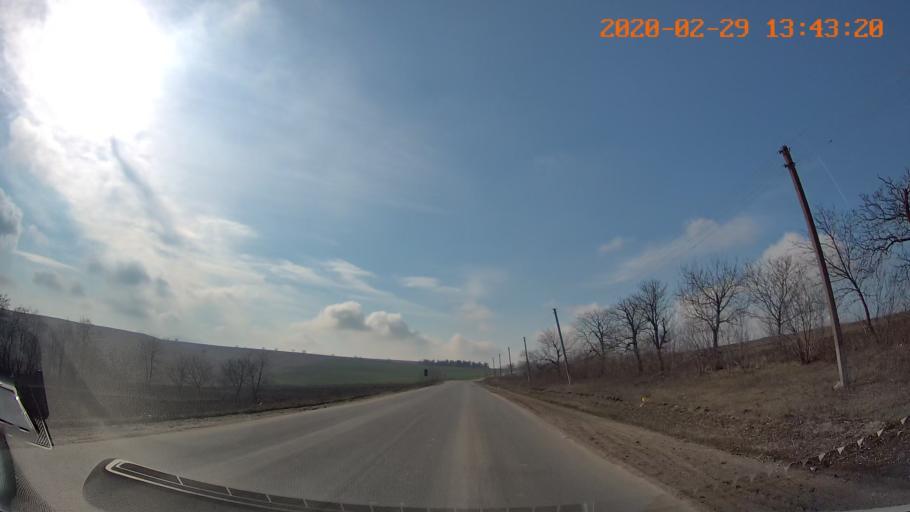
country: MD
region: Floresti
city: Leninskiy
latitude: 47.8401
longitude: 28.5341
